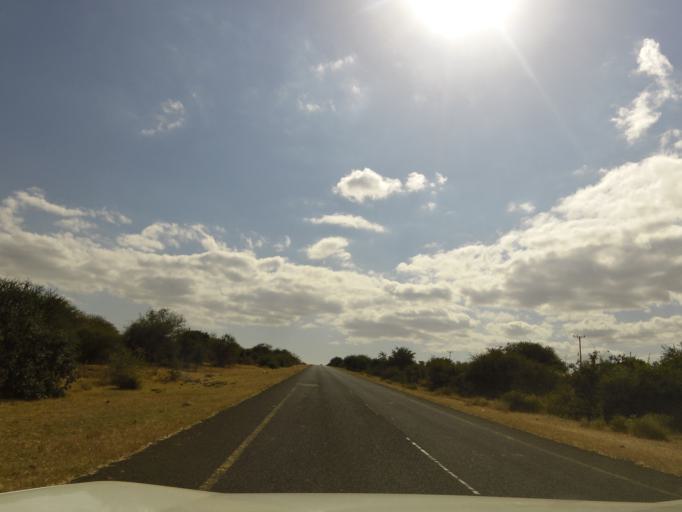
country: TZ
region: Arusha
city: Mto wa Mbu
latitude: -3.5215
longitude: 36.0479
